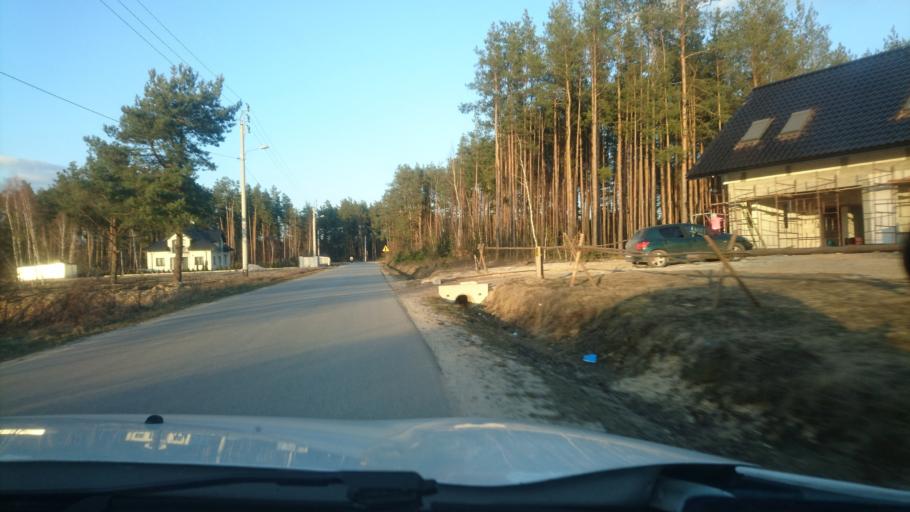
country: PL
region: Swietokrzyskie
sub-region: Powiat kielecki
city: Pierzchnica
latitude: 50.7783
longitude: 20.7106
